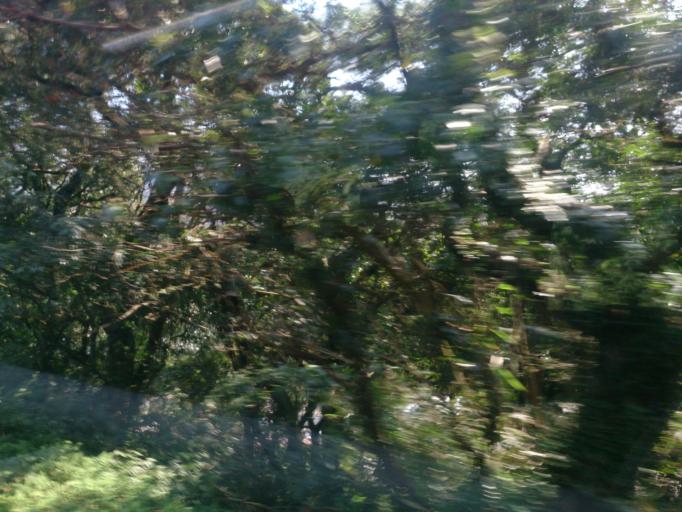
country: TW
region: Taipei
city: Taipei
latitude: 25.1799
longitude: 121.5430
